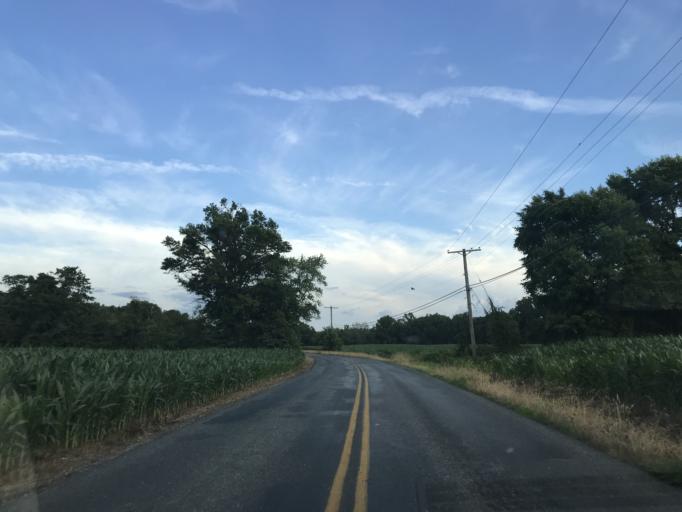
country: US
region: Maryland
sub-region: Harford County
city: Riverside
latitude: 39.5365
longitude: -76.2251
